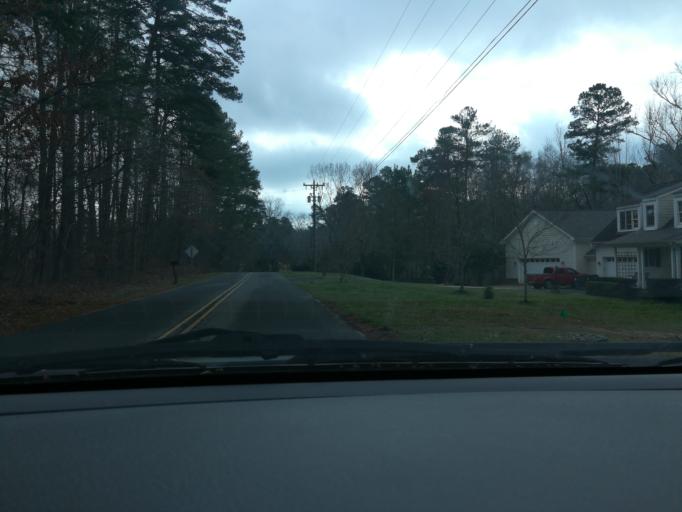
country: US
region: North Carolina
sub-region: Durham County
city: Durham
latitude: 36.0691
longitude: -78.9730
